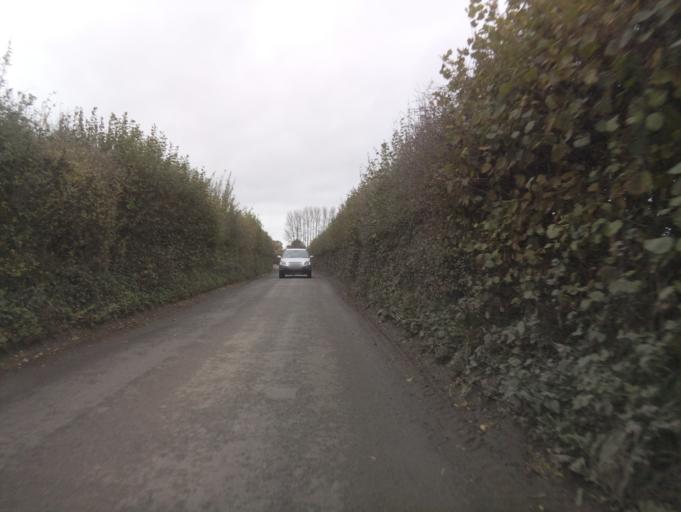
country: GB
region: England
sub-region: Somerset
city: South Petherton
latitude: 50.9340
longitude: -2.8278
